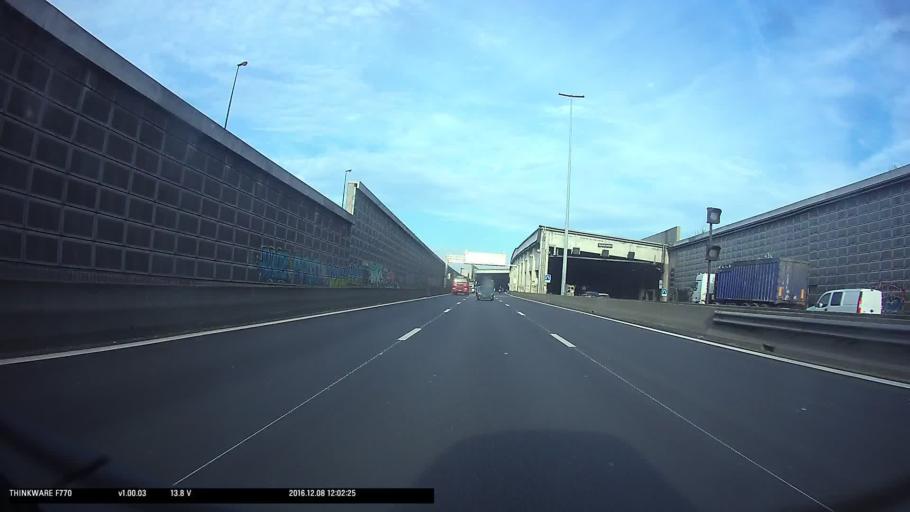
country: FR
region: Ile-de-France
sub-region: Departement de Seine-Saint-Denis
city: Le Bourget
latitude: 48.9182
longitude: 2.4288
